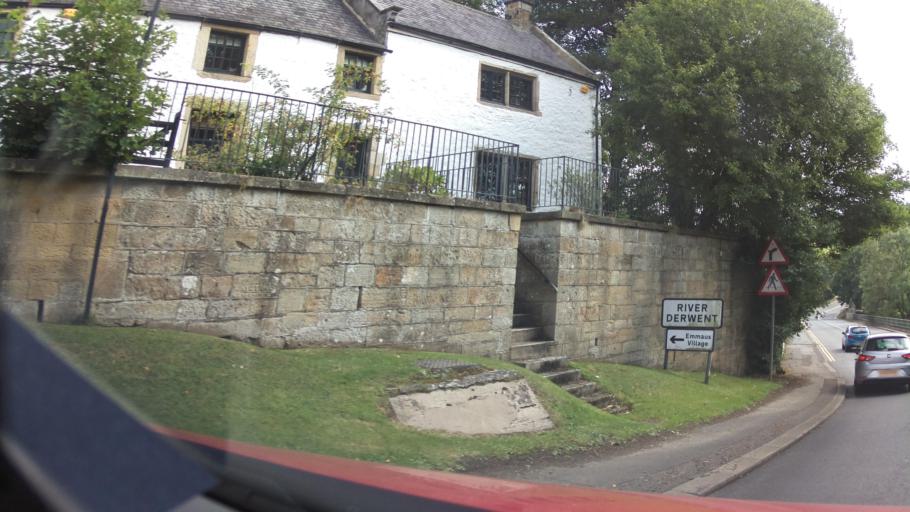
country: GB
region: England
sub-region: County Durham
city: Castleside
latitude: 54.8478
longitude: -1.8828
